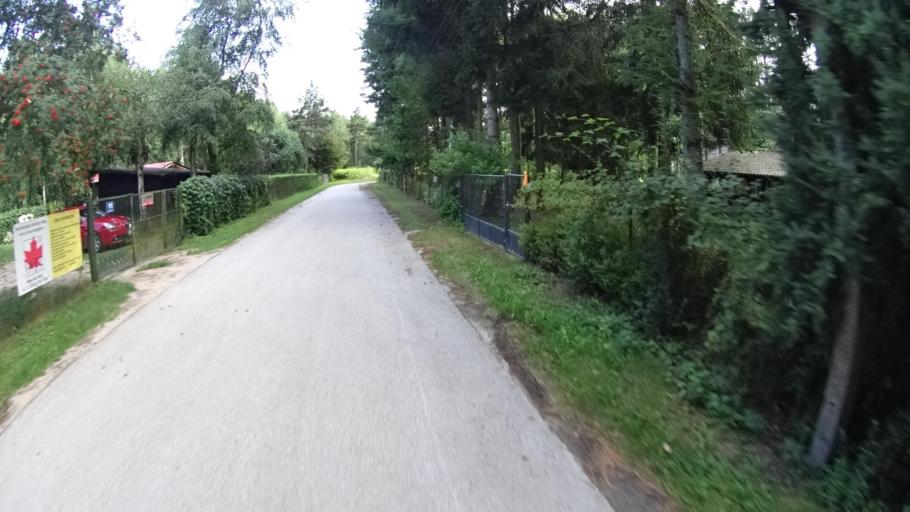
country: PL
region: Masovian Voivodeship
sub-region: Powiat piaseczynski
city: Tarczyn
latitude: 51.9729
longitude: 20.8692
